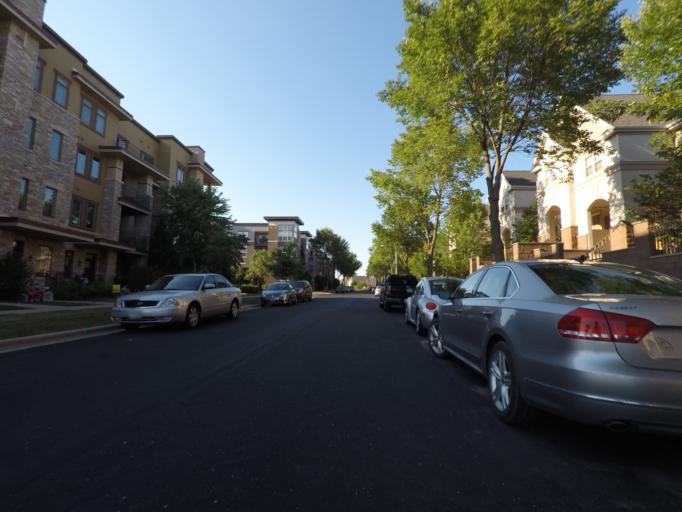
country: US
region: Wisconsin
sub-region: Dane County
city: Verona
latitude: 43.0324
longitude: -89.5238
